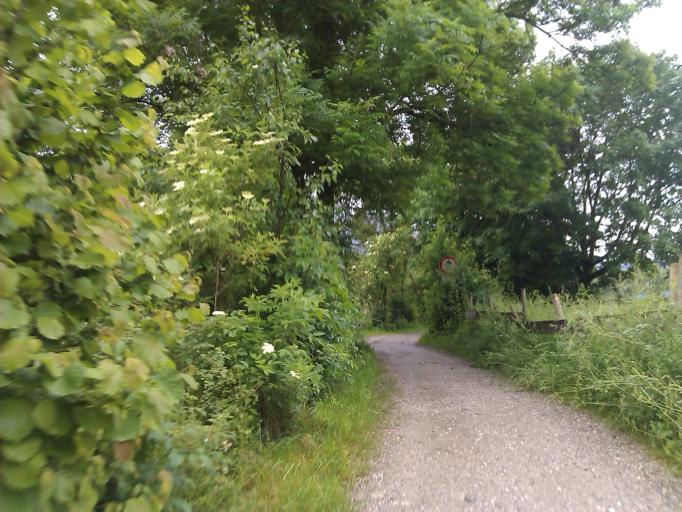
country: DE
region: Bavaria
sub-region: Swabia
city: Schwangau
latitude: 47.6017
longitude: 10.7133
